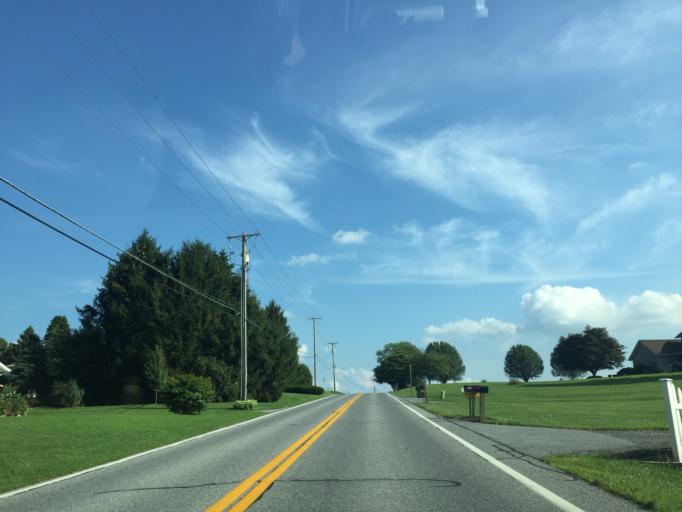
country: US
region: Maryland
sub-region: Carroll County
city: Hampstead
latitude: 39.6375
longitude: -76.7982
